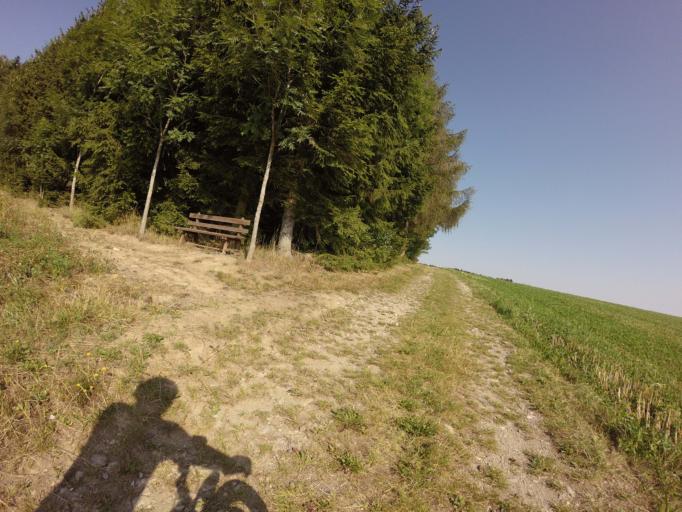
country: AT
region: Upper Austria
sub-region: Politischer Bezirk Urfahr-Umgebung
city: Bad Leonfelden
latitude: 48.5508
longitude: 14.3219
